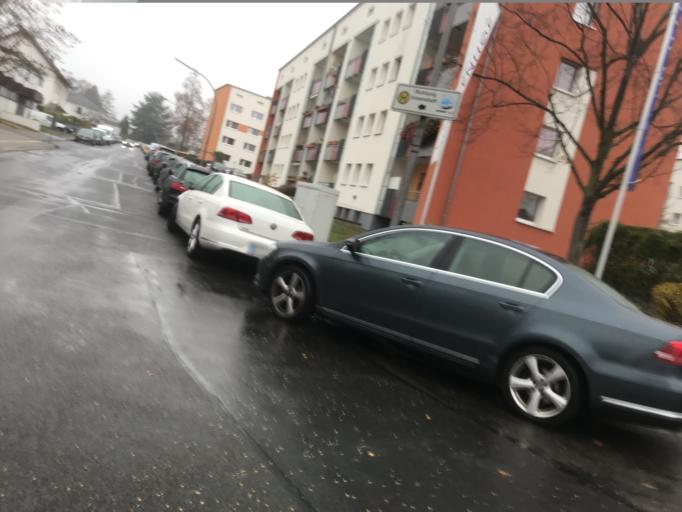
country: DE
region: Rheinland-Pfalz
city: Budenheim
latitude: 50.0455
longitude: 8.1901
